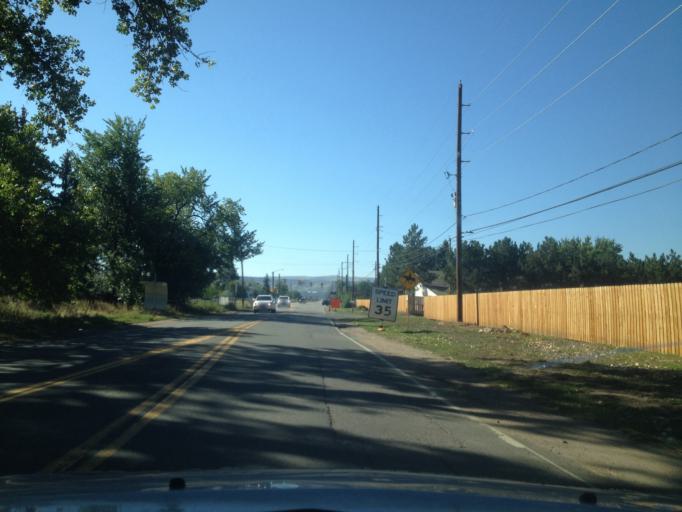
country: US
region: Colorado
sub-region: Jefferson County
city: Applewood
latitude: 39.7962
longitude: -105.1747
